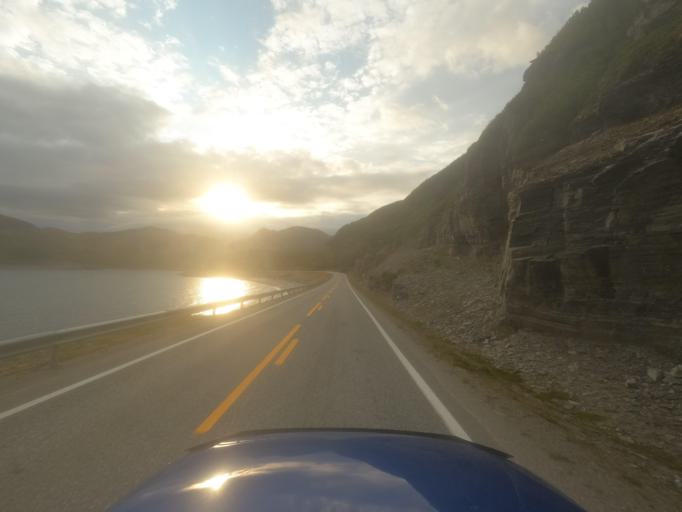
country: NO
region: Finnmark Fylke
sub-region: Nordkapp
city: Honningsvag
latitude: 70.6718
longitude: 25.4286
